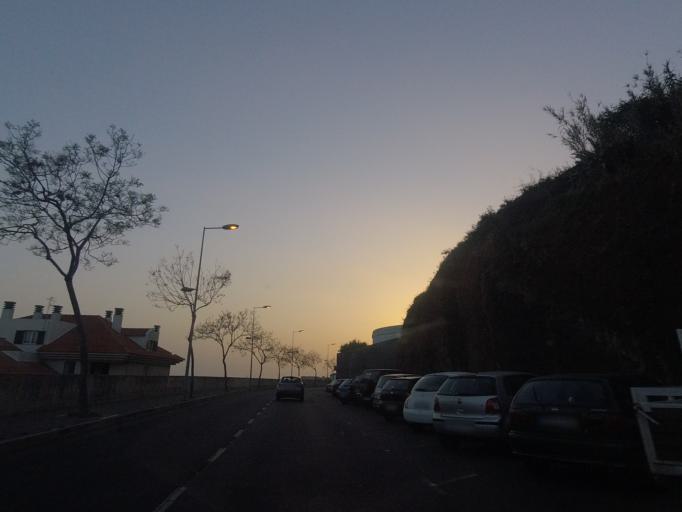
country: PT
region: Madeira
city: Camara de Lobos
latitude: 32.6400
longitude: -16.9346
